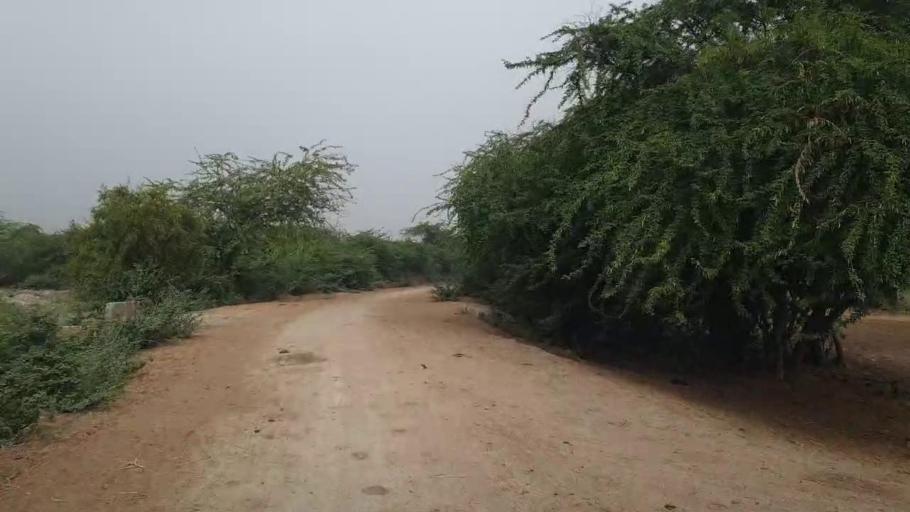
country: PK
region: Sindh
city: Badin
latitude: 24.5747
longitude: 68.6663
